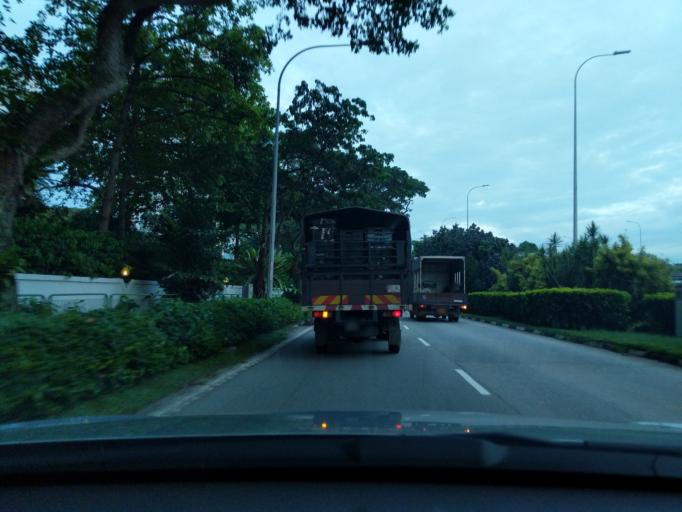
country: SG
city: Singapore
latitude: 1.2960
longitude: 103.8829
